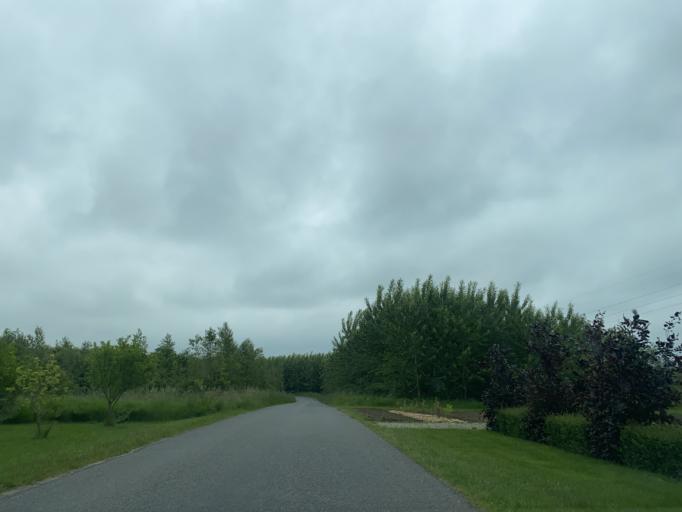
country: DK
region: Central Jutland
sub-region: Viborg Kommune
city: Bjerringbro
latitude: 56.3372
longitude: 9.6629
